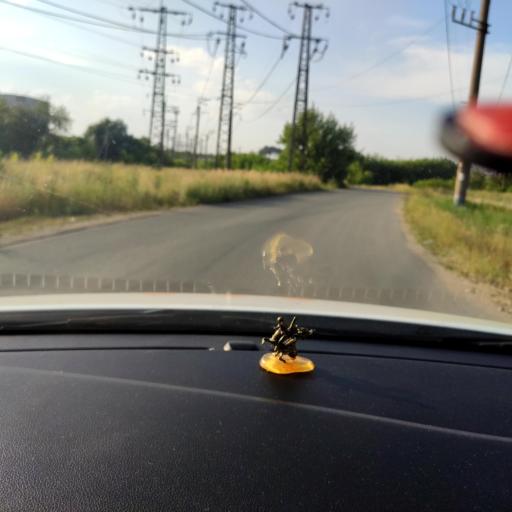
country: RU
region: Tatarstan
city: Staroye Arakchino
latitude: 55.8132
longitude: 48.9117
